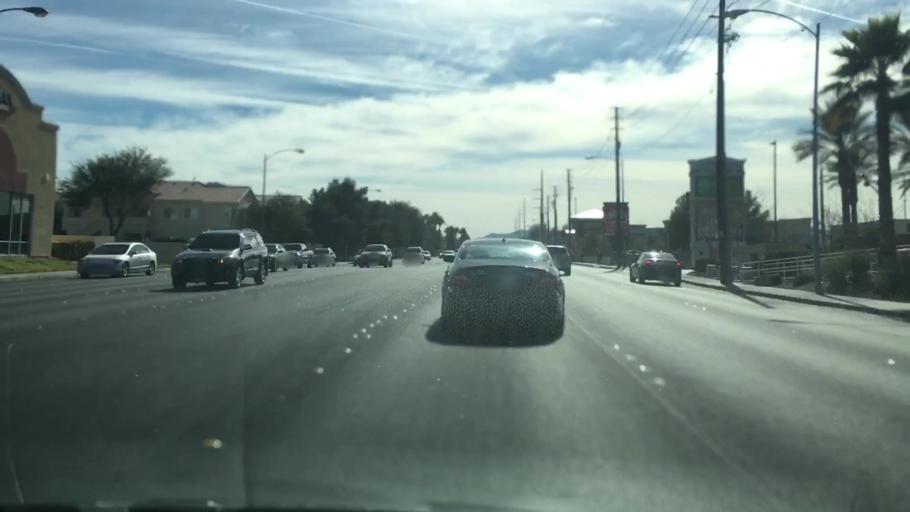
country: US
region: Nevada
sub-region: Clark County
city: Whitney
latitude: 36.0558
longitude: -115.1184
